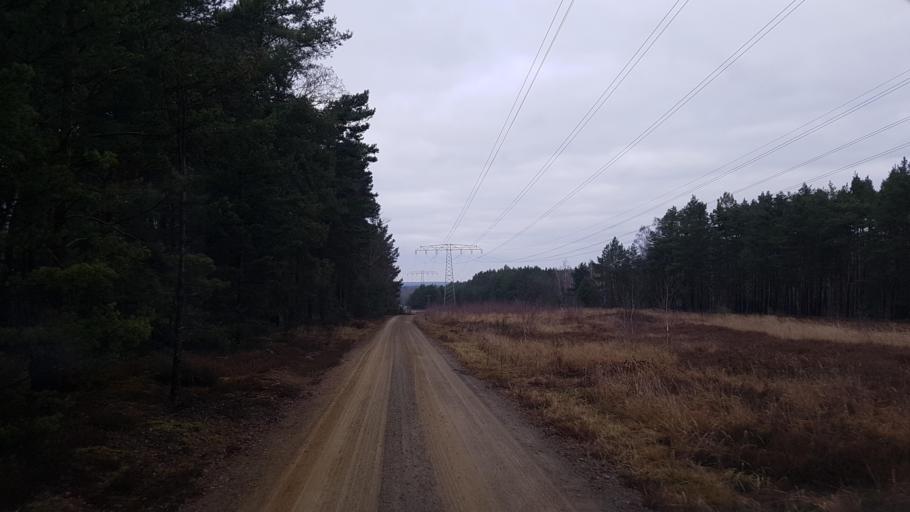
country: DE
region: Brandenburg
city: Altdobern
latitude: 51.6427
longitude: 14.0049
